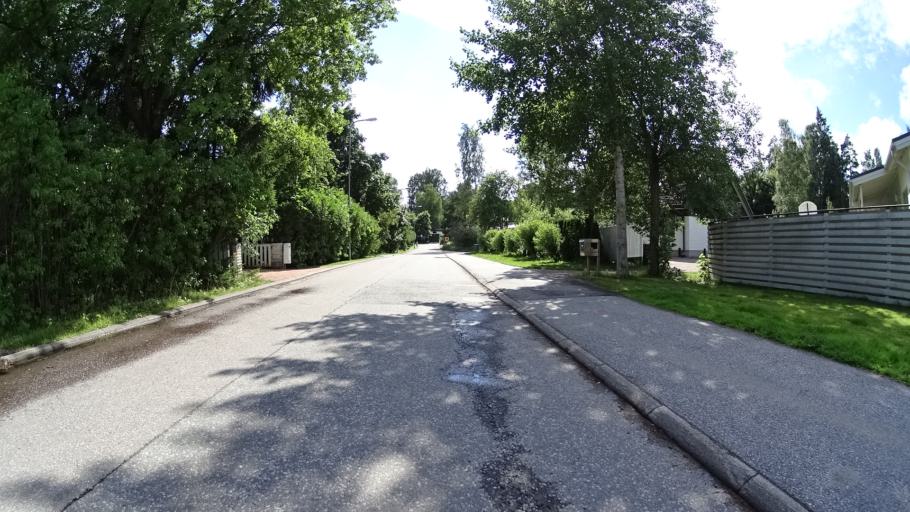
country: FI
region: Uusimaa
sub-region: Helsinki
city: Kilo
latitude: 60.1994
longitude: 24.7676
